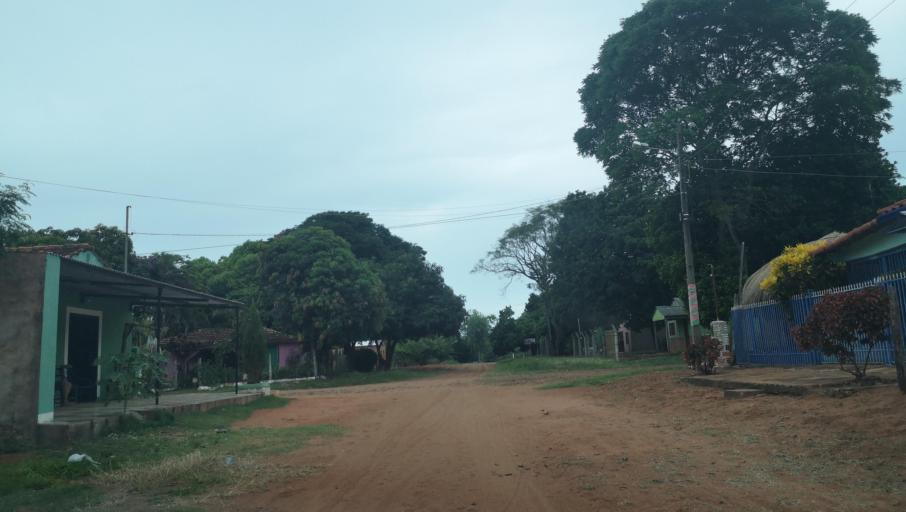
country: PY
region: San Pedro
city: Capiibary
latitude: -24.7267
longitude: -56.0121
